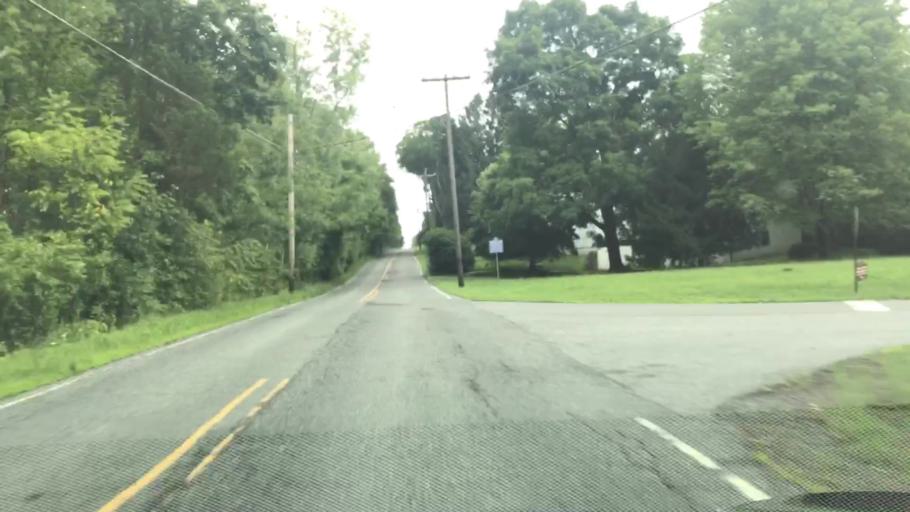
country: US
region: New Jersey
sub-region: Hunterdon County
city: Annandale
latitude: 40.6512
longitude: -74.8614
